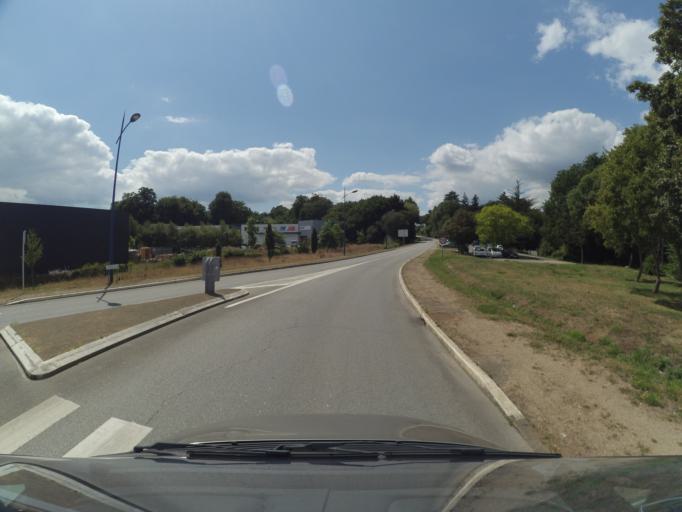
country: FR
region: Brittany
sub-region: Departement du Morbihan
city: Landevant
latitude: 47.7582
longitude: -3.1335
